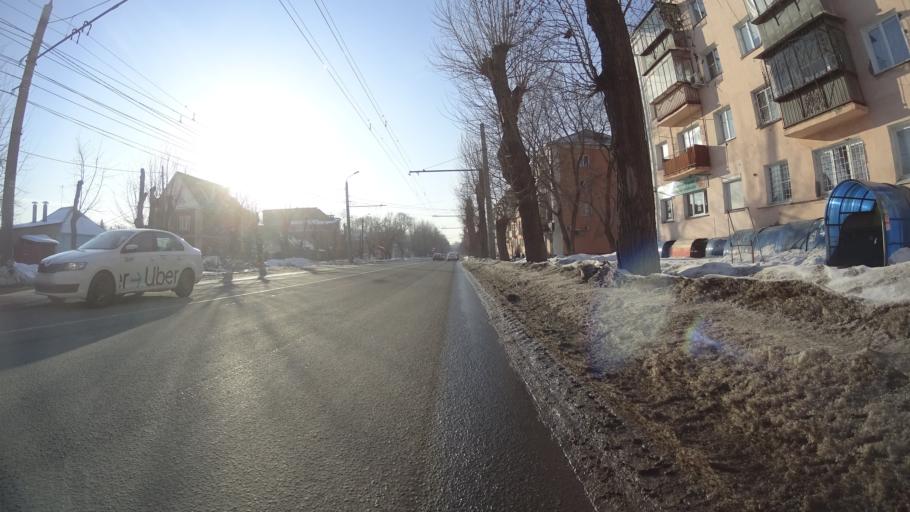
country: RU
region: Chelyabinsk
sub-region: Gorod Chelyabinsk
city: Chelyabinsk
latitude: 55.1817
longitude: 61.4482
